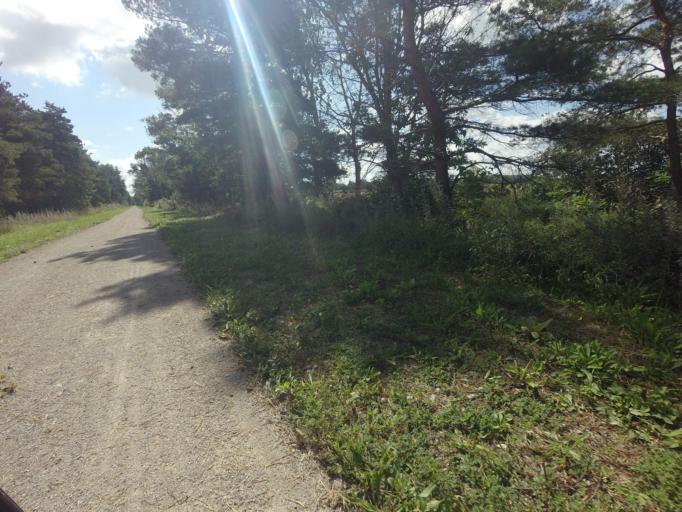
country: CA
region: Ontario
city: Huron East
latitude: 43.6834
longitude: -81.3071
